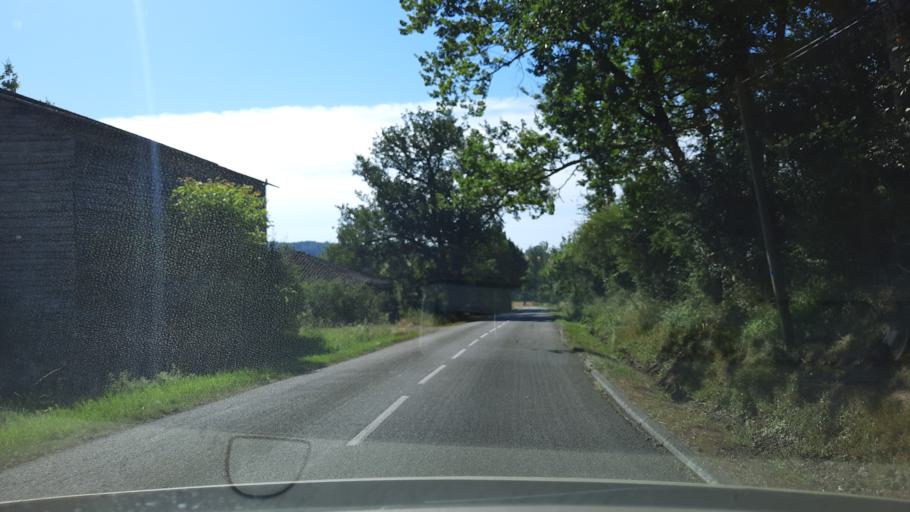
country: FR
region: Midi-Pyrenees
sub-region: Departement du Tarn-et-Garonne
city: Molieres
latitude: 44.1930
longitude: 1.4475
